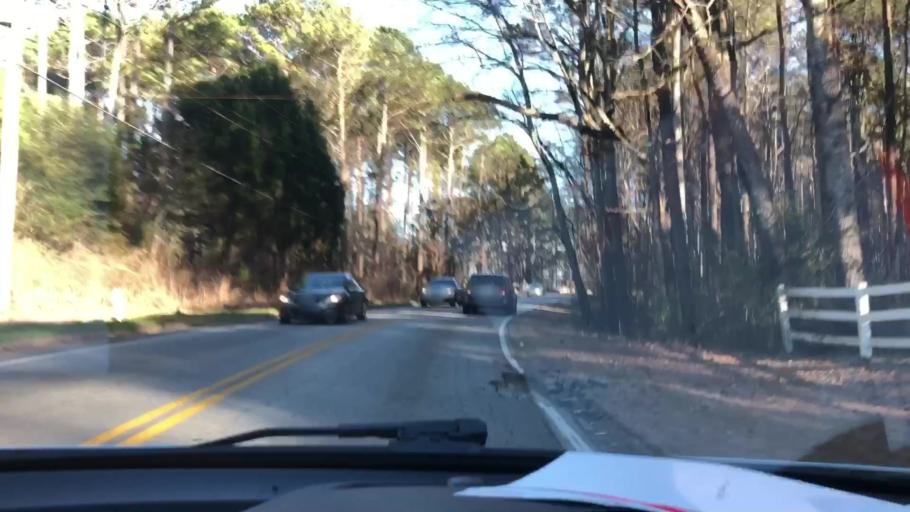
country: US
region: Georgia
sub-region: Gwinnett County
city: Mountain Park
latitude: 33.8302
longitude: -84.1464
